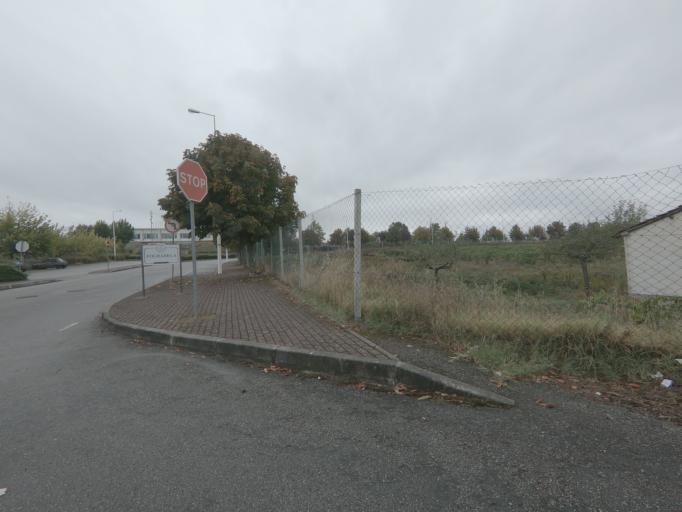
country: PT
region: Vila Real
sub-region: Vila Real
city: Vila Real
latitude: 41.2854
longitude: -7.7348
